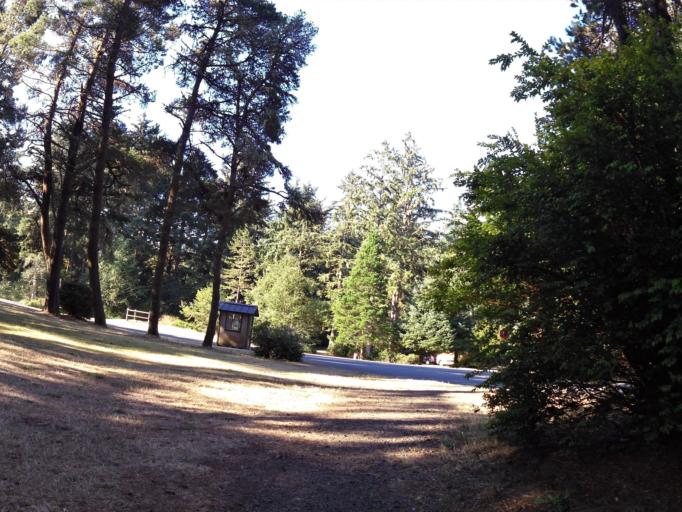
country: US
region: Oregon
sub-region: Clatsop County
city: Warrenton
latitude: 46.1824
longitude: -123.9635
